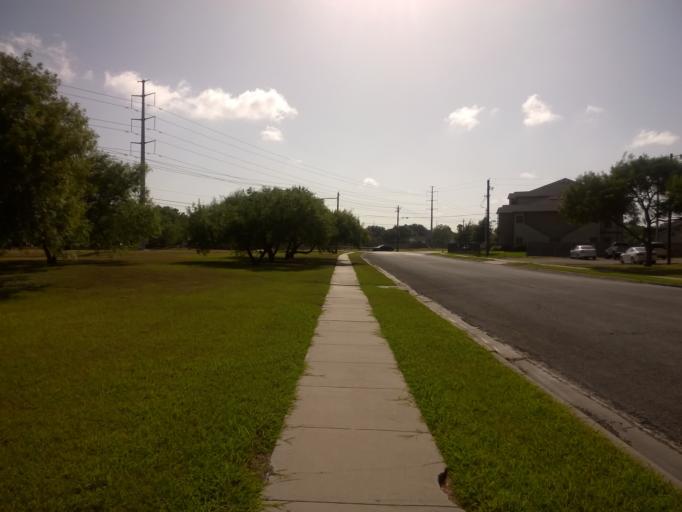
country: US
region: Texas
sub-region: Nueces County
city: Corpus Christi
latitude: 27.6896
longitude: -97.3659
